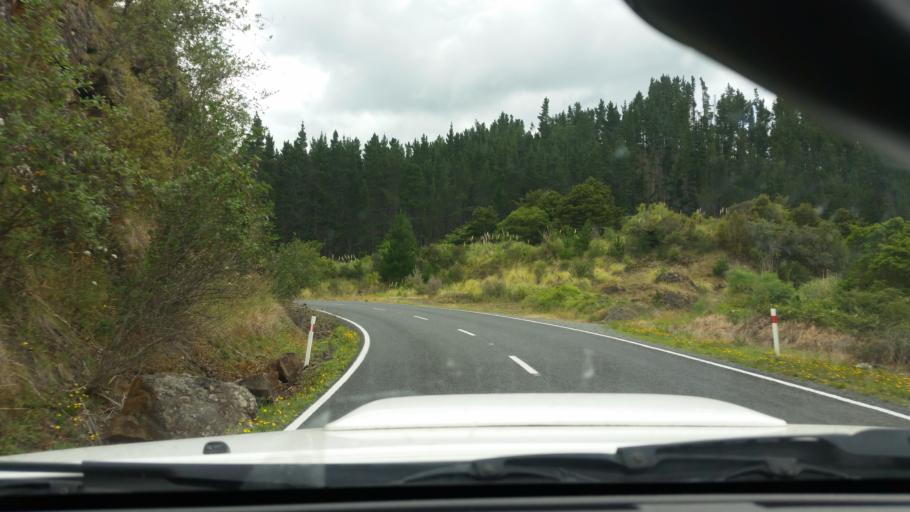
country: NZ
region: Northland
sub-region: Kaipara District
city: Dargaville
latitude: -35.7657
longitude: 173.9065
